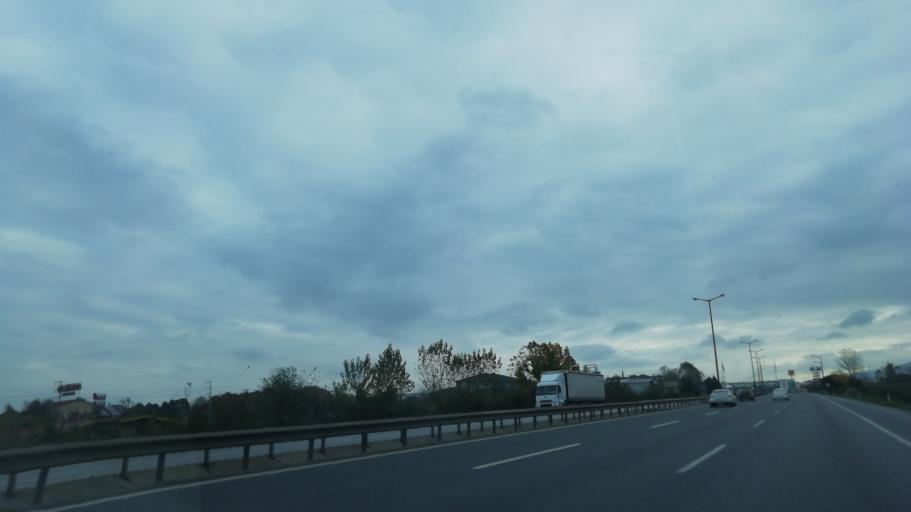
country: TR
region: Kocaeli
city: Derbent
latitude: 40.7297
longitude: 30.0623
